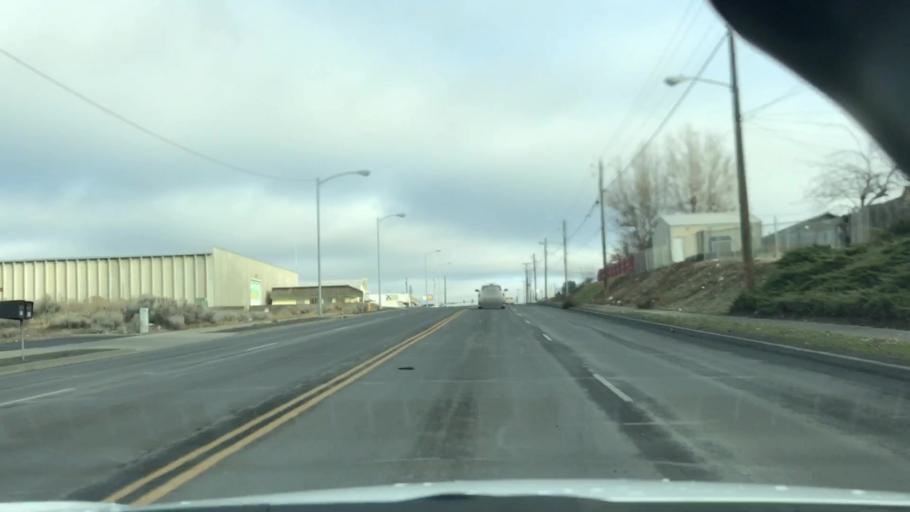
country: US
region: Washington
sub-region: Grant County
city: Moses Lake
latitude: 47.1311
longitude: -119.2619
